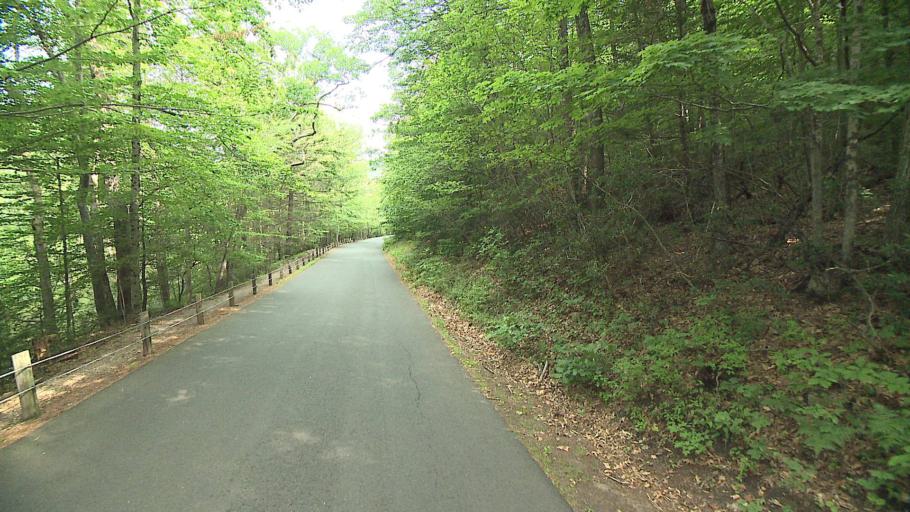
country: US
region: Connecticut
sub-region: Litchfield County
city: New Hartford Center
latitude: 41.9355
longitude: -73.0004
